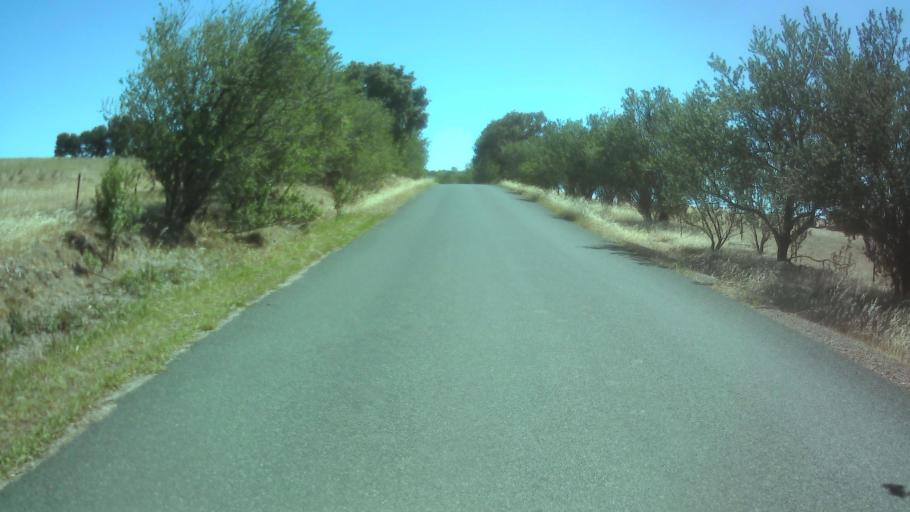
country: AU
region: New South Wales
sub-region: Weddin
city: Grenfell
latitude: -33.9699
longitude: 148.4057
